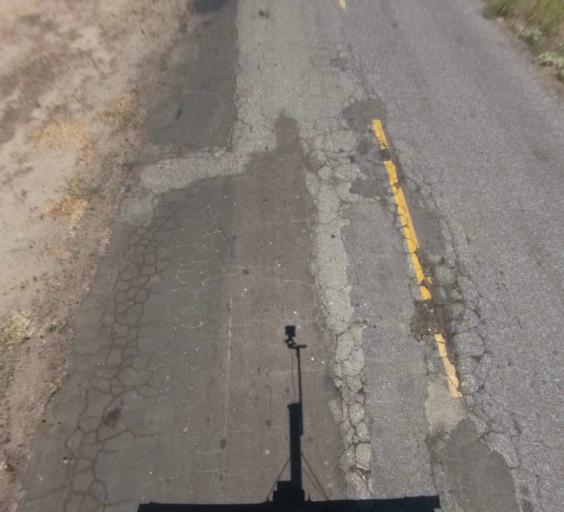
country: US
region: California
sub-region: Madera County
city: Madera Acres
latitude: 37.0576
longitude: -120.0293
